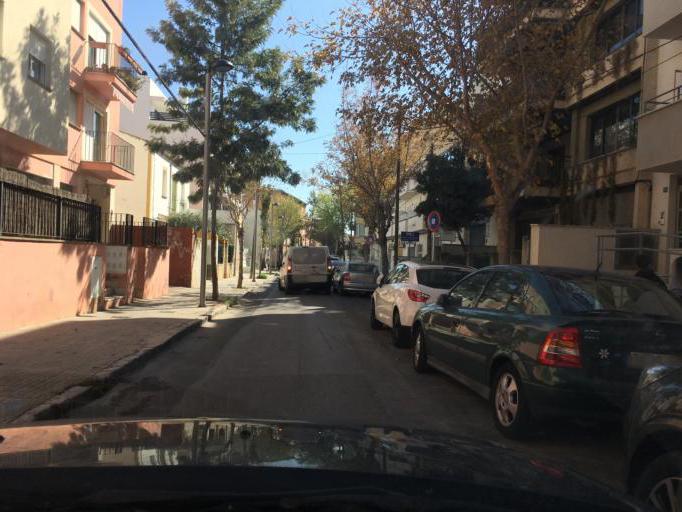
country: ES
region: Balearic Islands
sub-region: Illes Balears
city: Palma
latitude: 39.5844
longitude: 2.6758
